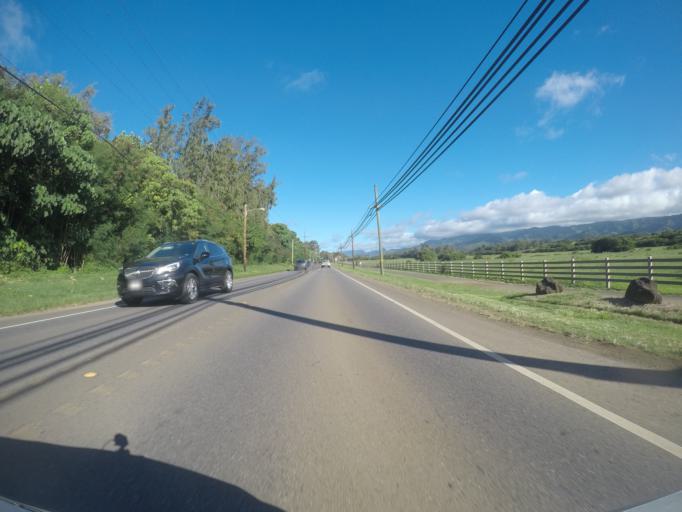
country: US
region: Hawaii
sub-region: Honolulu County
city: La'ie
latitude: 21.6618
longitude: -157.9345
